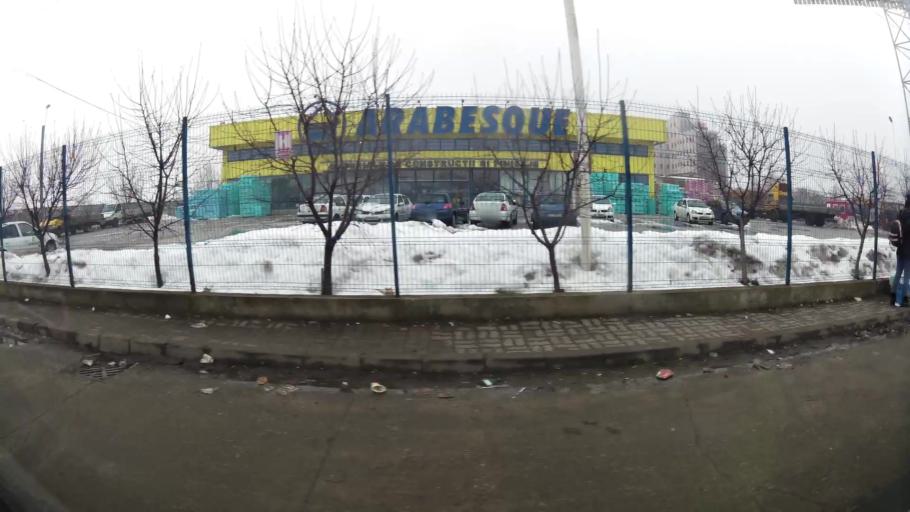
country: RO
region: Ilfov
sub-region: Comuna Chiajna
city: Rosu
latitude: 44.4358
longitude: 25.9874
